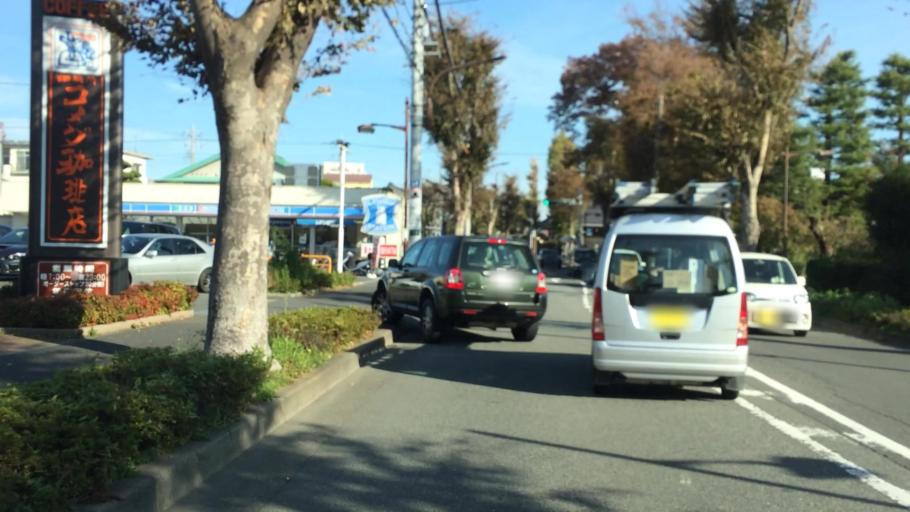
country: JP
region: Tokyo
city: Chofugaoka
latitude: 35.6652
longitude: 139.5148
